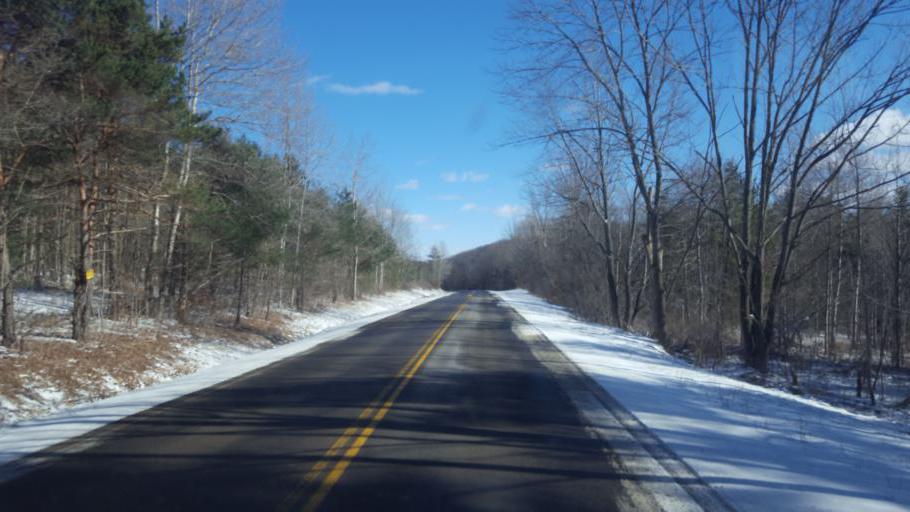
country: US
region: New York
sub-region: Allegany County
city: Belmont
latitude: 42.1709
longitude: -78.0572
